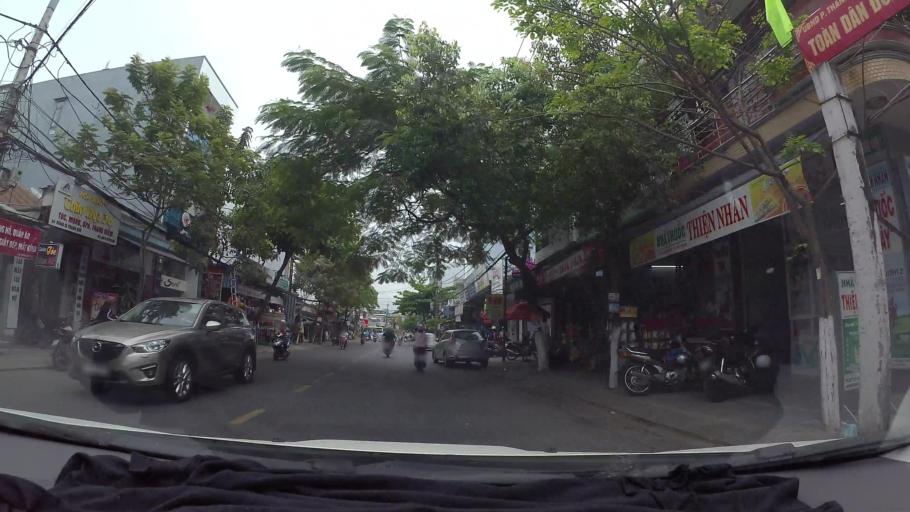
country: VN
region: Da Nang
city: Thanh Khe
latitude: 16.0683
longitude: 108.1816
